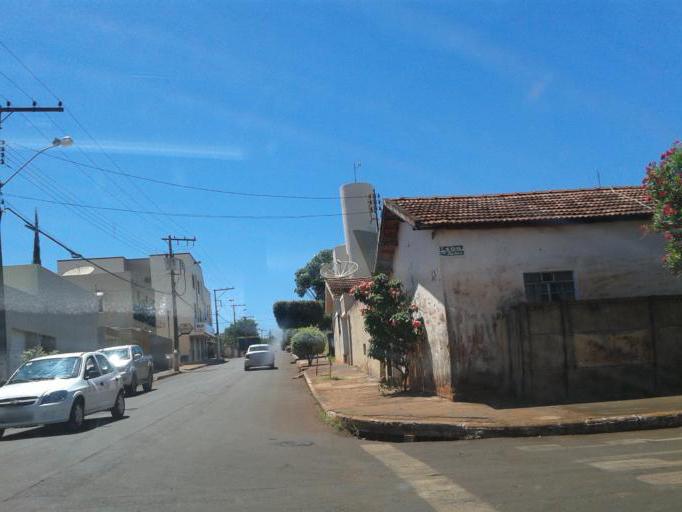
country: BR
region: Minas Gerais
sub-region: Capinopolis
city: Capinopolis
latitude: -18.6828
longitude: -49.5686
